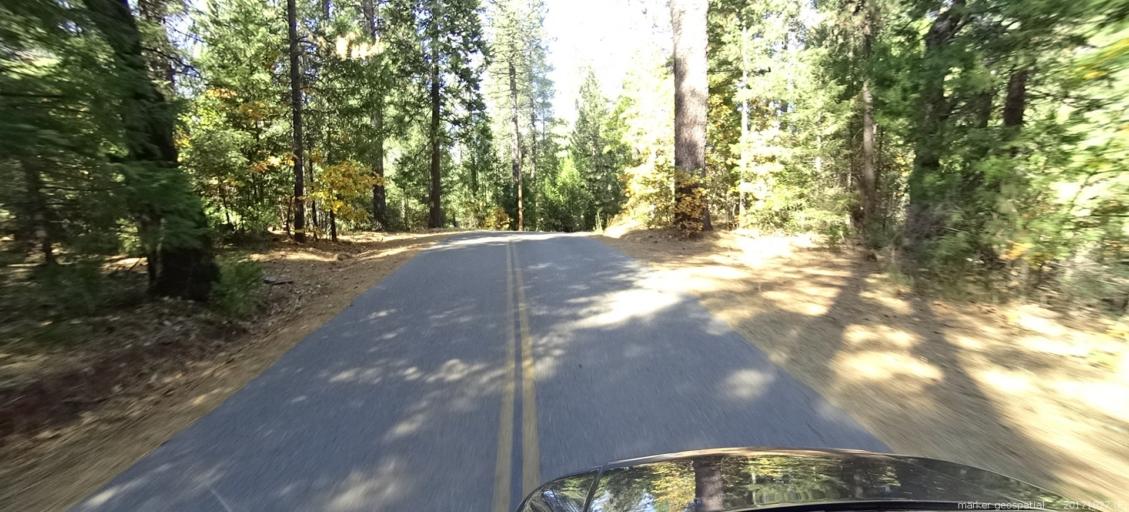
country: US
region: California
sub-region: Shasta County
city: Shingletown
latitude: 40.7403
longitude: -121.9277
